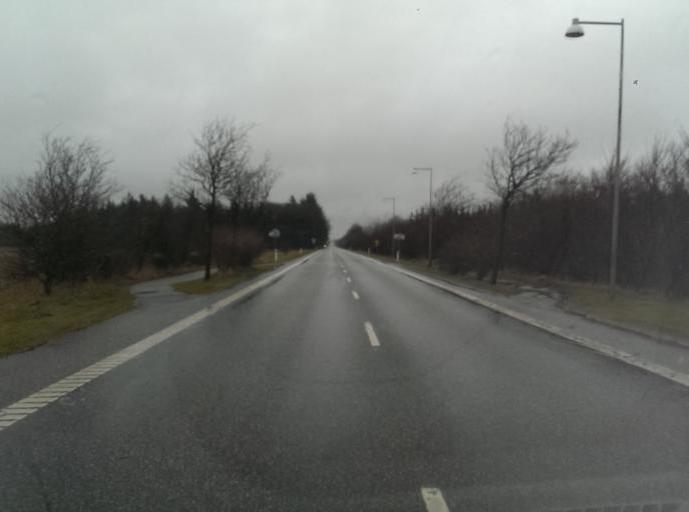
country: DK
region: Central Jutland
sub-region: Ringkobing-Skjern Kommune
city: Tarm
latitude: 55.8035
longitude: 8.4924
